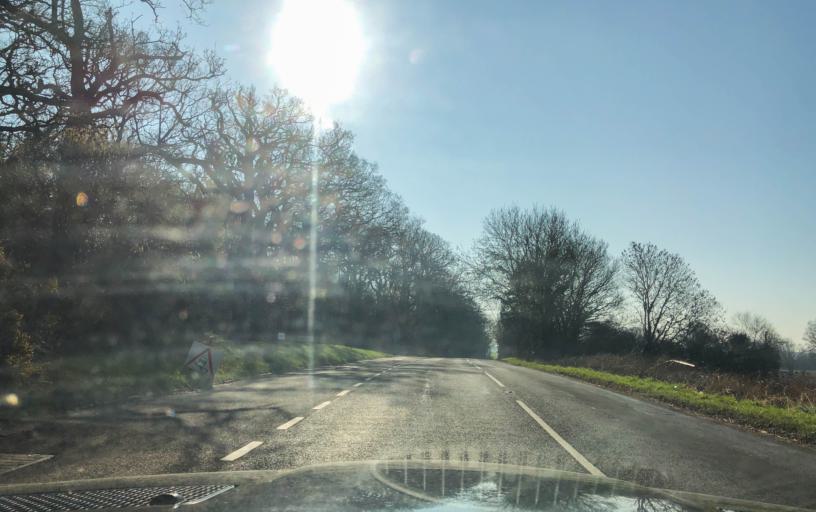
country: GB
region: England
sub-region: Warwickshire
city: Warwick
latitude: 52.2339
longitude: -1.5605
